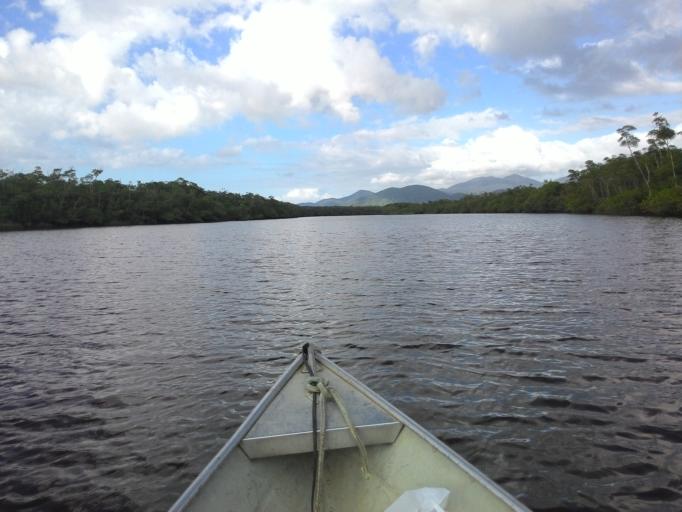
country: BR
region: Sao Paulo
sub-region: Pariquera-Acu
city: Pariquera Acu
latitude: -24.8294
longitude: -47.7379
